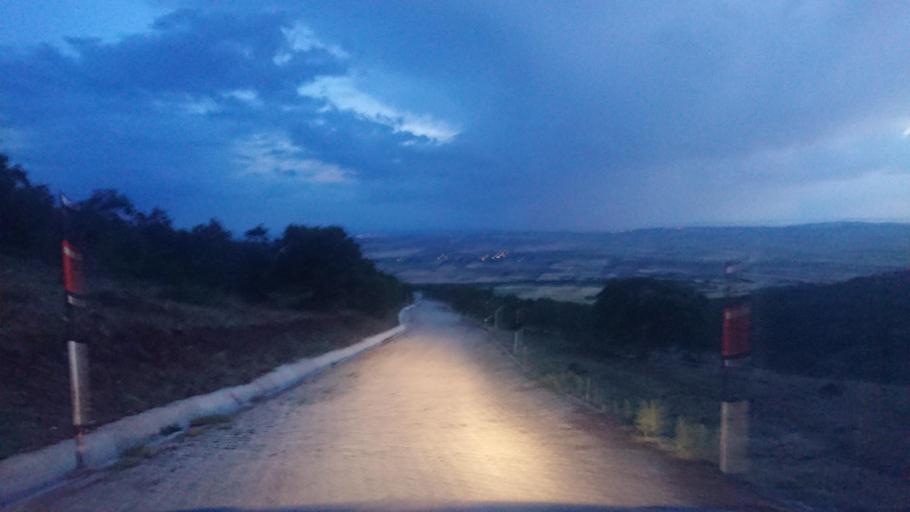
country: TR
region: Aksaray
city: Ortakoy
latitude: 38.6434
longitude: 34.0226
